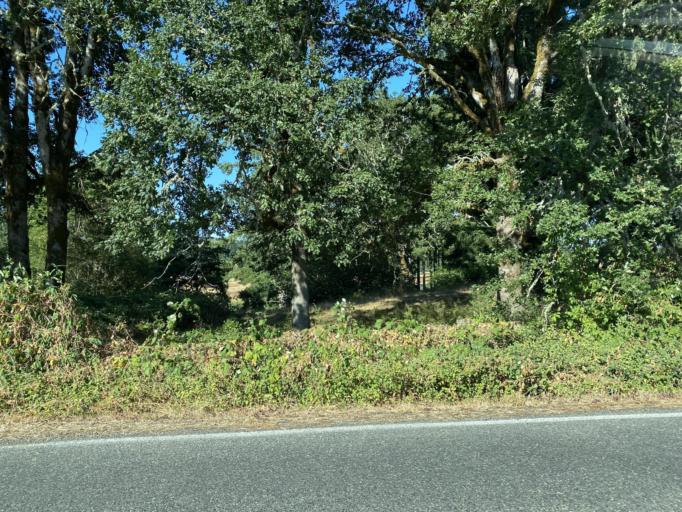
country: US
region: Washington
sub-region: Thurston County
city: Rainier
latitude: 46.8966
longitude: -122.7551
